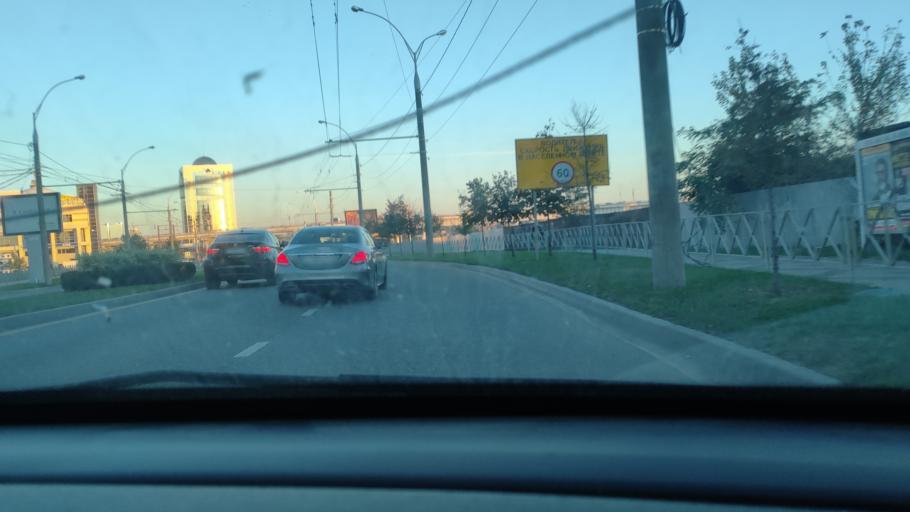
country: RU
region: Krasnodarskiy
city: Krasnodar
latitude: 45.0378
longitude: 38.9502
